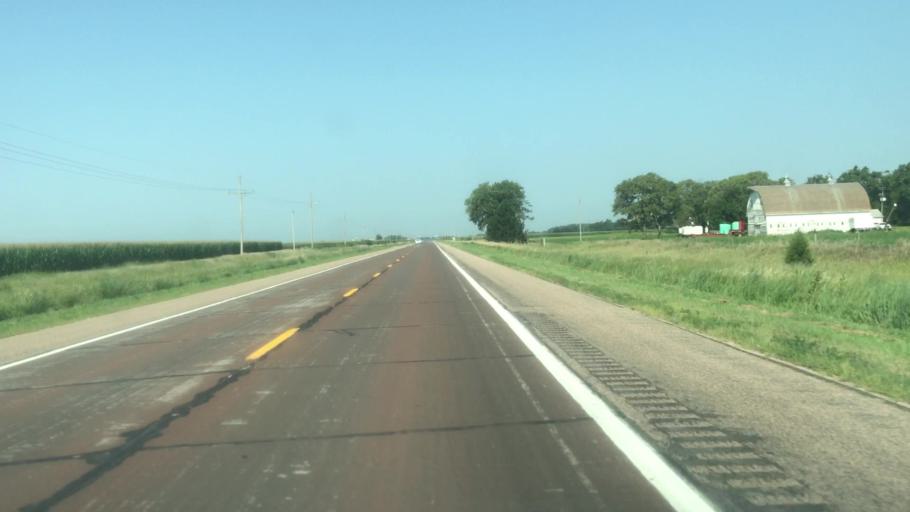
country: US
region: Nebraska
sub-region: Hall County
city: Grand Island
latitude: 40.9674
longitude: -98.4529
